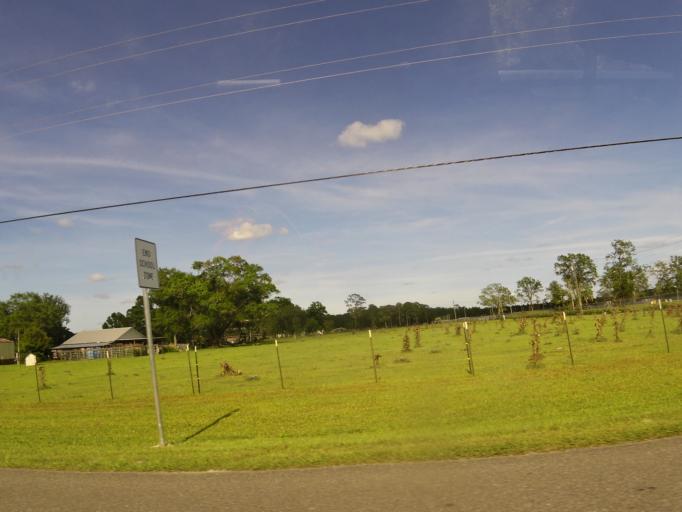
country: US
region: Florida
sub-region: Nassau County
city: Callahan
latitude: 30.5534
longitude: -81.8843
